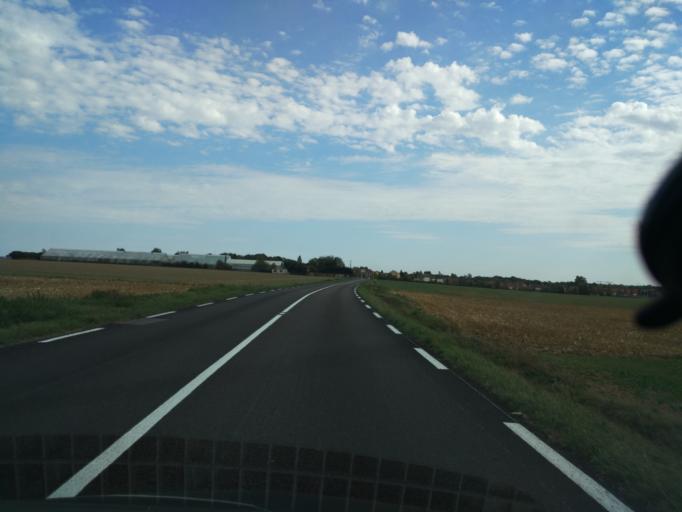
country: FR
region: Ile-de-France
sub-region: Departement de l'Essonne
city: Gometz-la-Ville
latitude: 48.6738
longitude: 2.1131
